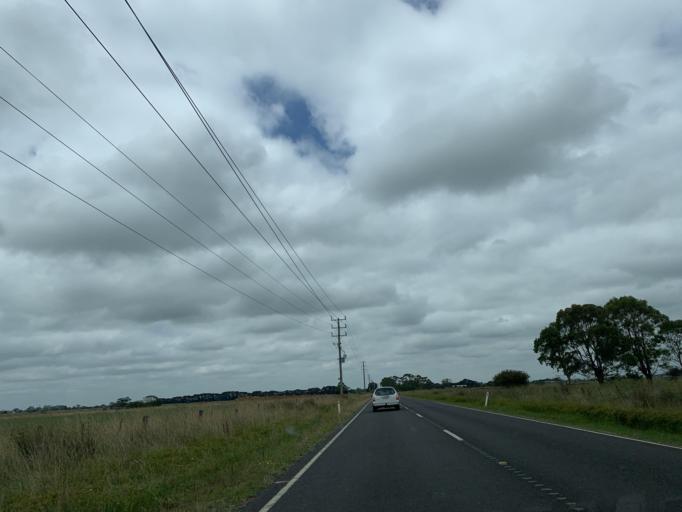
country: AU
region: Victoria
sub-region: Wellington
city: Heyfield
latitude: -37.9898
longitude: 146.8752
